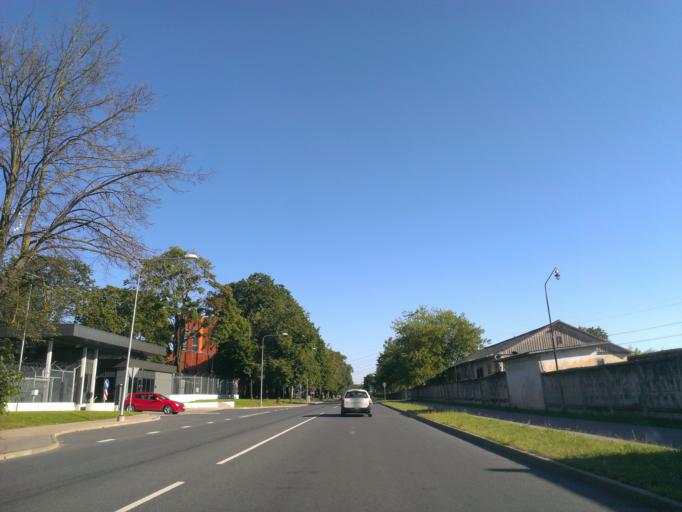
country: LV
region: Riga
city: Jaunciems
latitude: 56.9880
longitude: 24.1899
